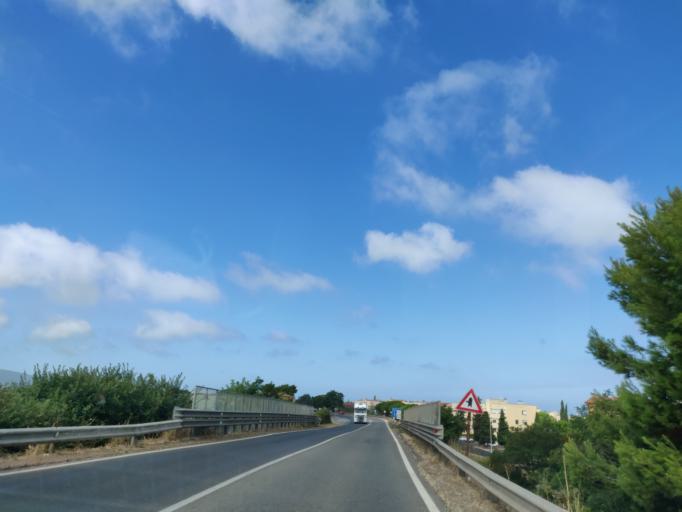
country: IT
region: Tuscany
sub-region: Provincia di Grosseto
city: Orbetello Scalo
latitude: 42.4463
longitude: 11.2531
